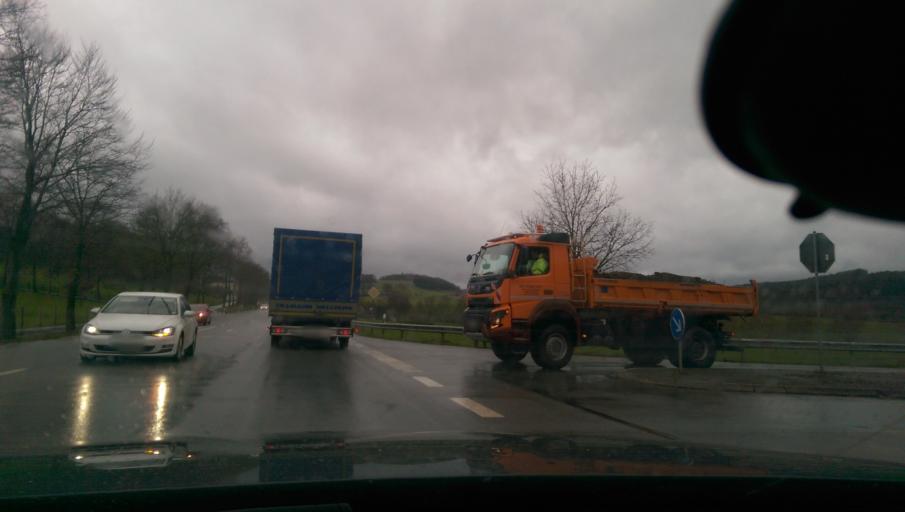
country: DE
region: North Rhine-Westphalia
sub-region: Regierungsbezirk Arnsberg
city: Sundern
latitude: 51.3101
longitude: 7.9940
